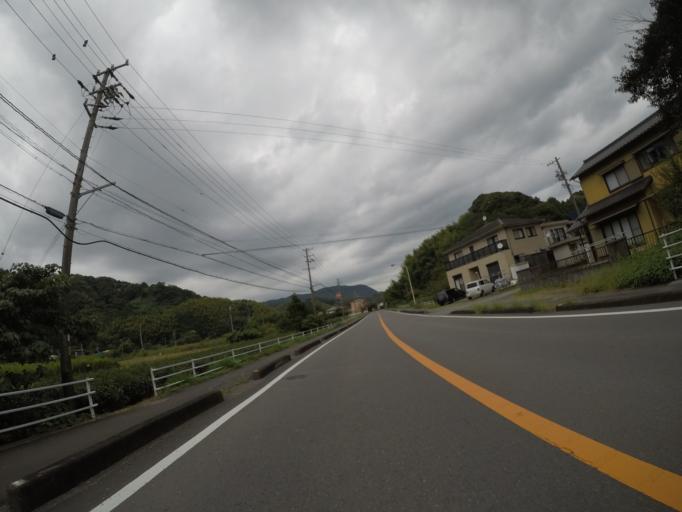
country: JP
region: Shizuoka
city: Fujieda
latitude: 34.9013
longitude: 138.2610
